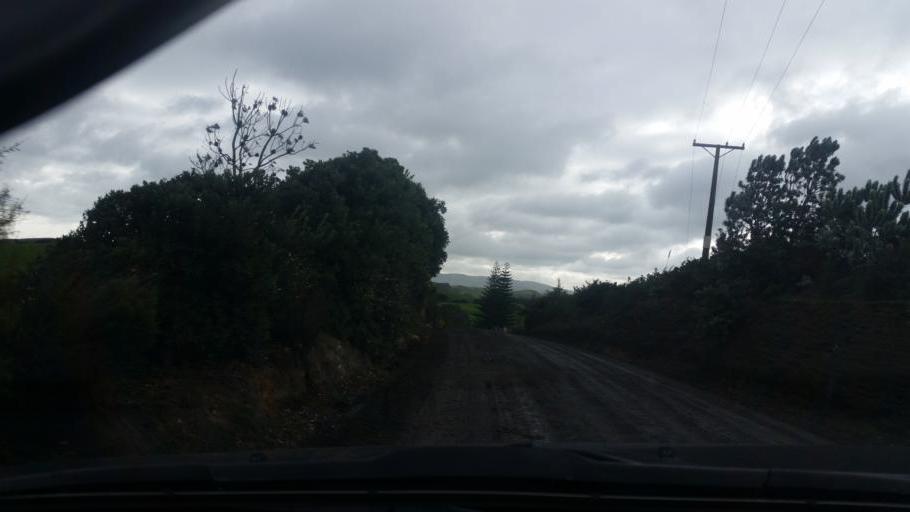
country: NZ
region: Northland
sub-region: Kaipara District
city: Dargaville
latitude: -35.8461
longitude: 173.6613
